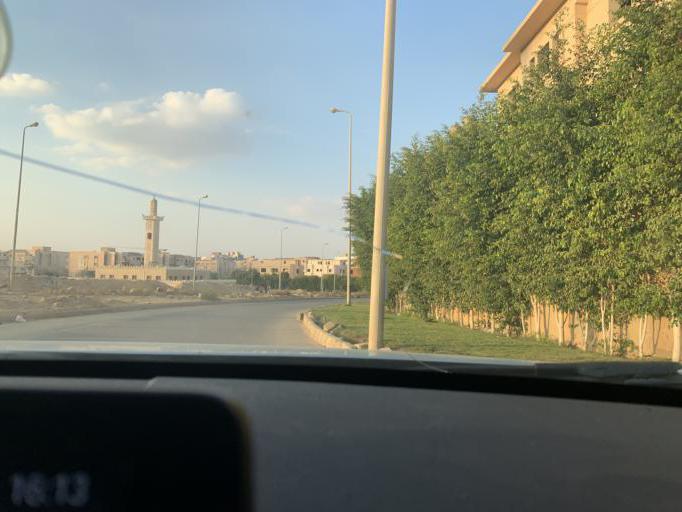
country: EG
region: Muhafazat al Qalyubiyah
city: Al Khankah
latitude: 30.0212
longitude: 31.4816
